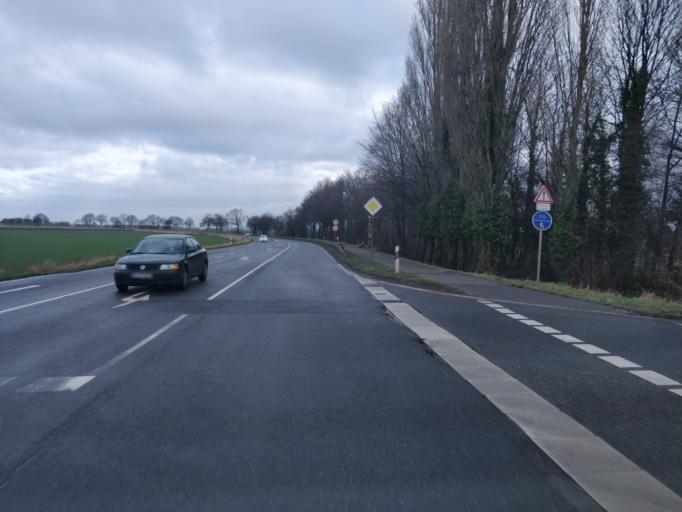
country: DE
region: North Rhine-Westphalia
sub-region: Regierungsbezirk Koln
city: Euskirchen
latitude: 50.6297
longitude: 6.8452
